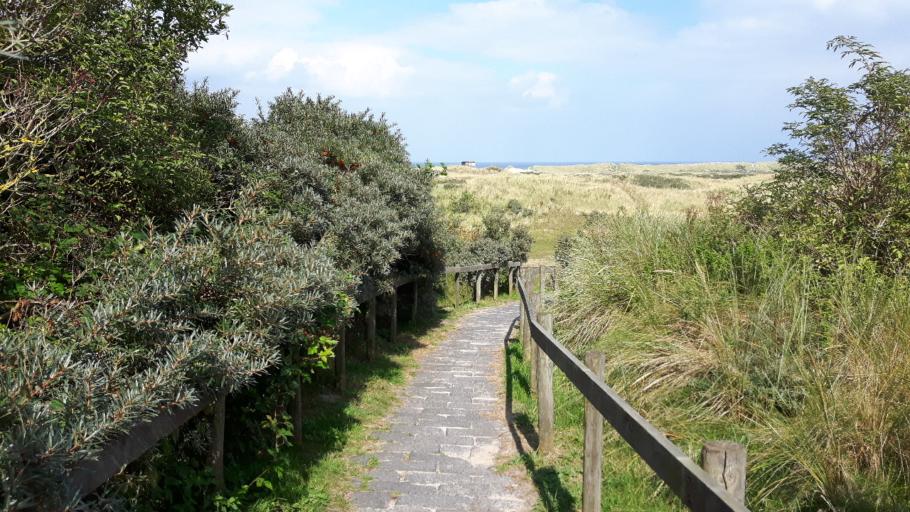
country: NL
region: Friesland
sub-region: Gemeente Dongeradeel
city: Holwerd
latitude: 53.4580
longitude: 5.9028
